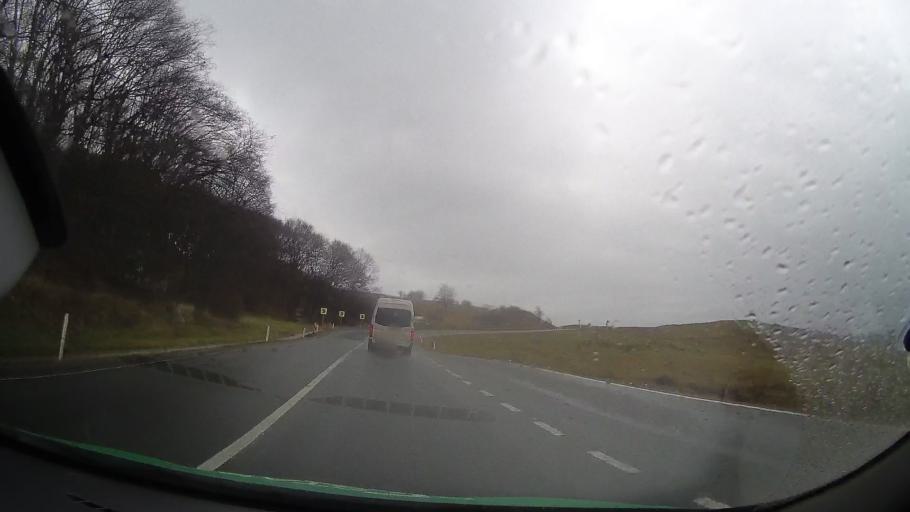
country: RO
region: Bistrita-Nasaud
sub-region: Comuna Galatii Bistritei
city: Galatii Bistritei
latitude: 47.0344
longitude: 24.4213
